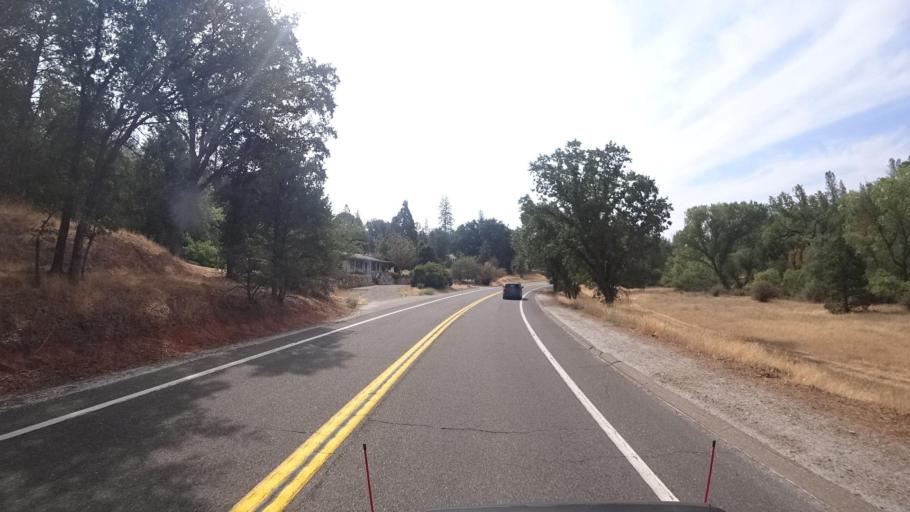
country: US
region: California
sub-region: Mariposa County
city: Midpines
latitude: 37.5597
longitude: -119.9338
